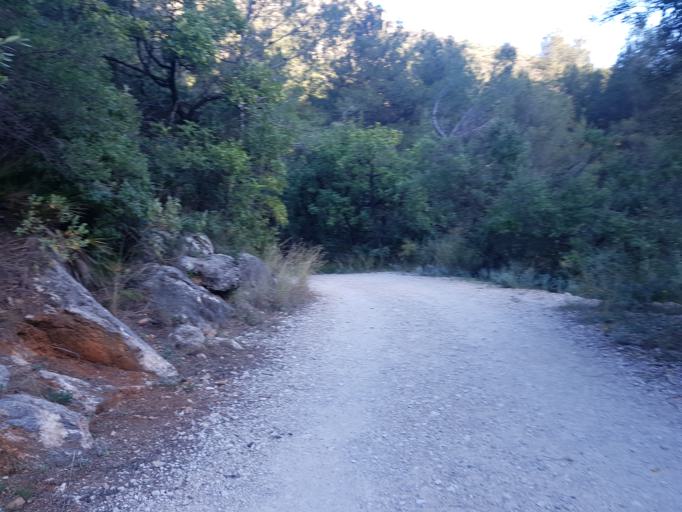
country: ES
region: Andalusia
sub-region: Provincia de Malaga
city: Marbella
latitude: 36.5392
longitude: -4.8843
